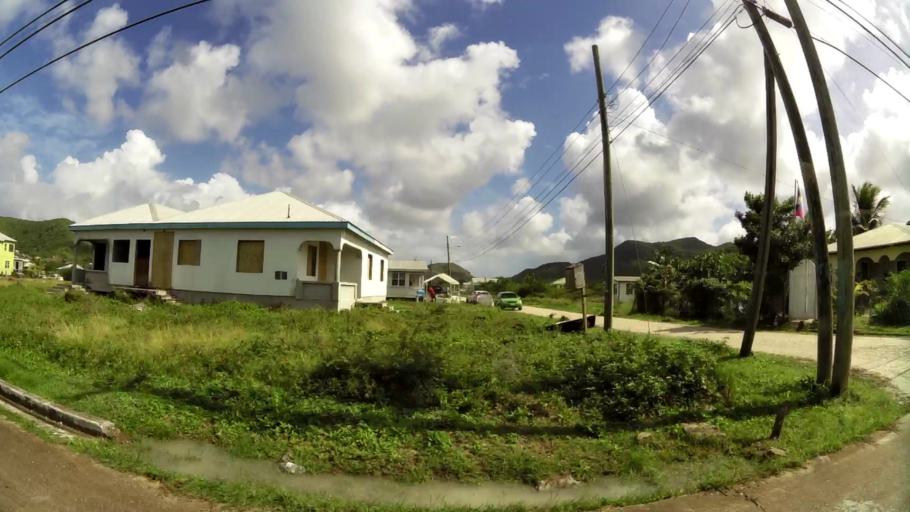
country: AG
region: Saint Mary
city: Bolands
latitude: 17.0713
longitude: -61.8742
